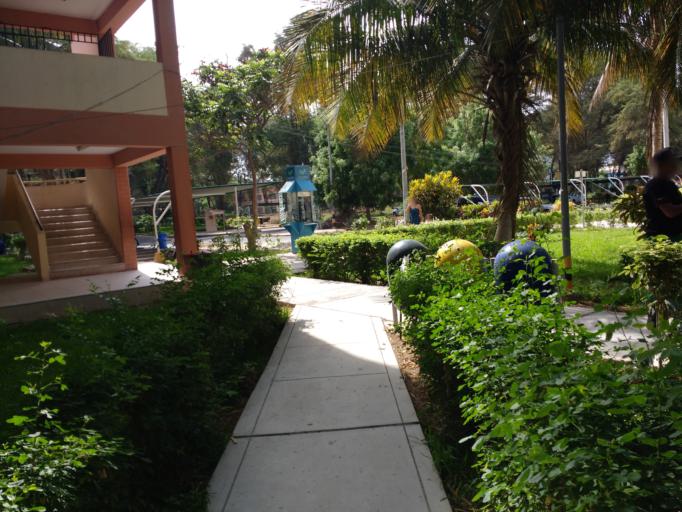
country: PE
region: Piura
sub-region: Provincia de Piura
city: Piura
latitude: -5.1793
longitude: -80.6209
